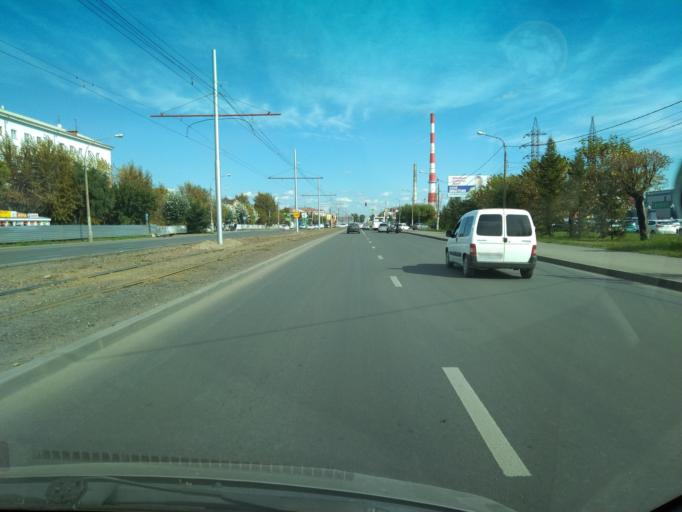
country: RU
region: Krasnoyarskiy
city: Berezovka
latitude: 56.0215
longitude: 93.0089
